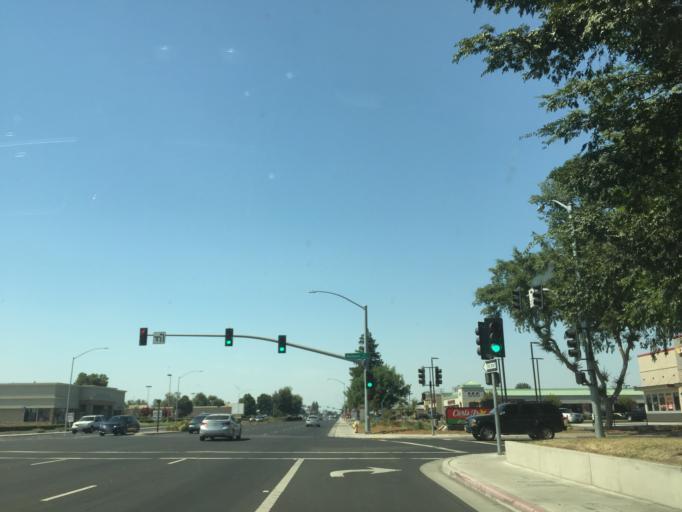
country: US
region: California
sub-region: Tulare County
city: Visalia
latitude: 36.2999
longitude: -119.3135
